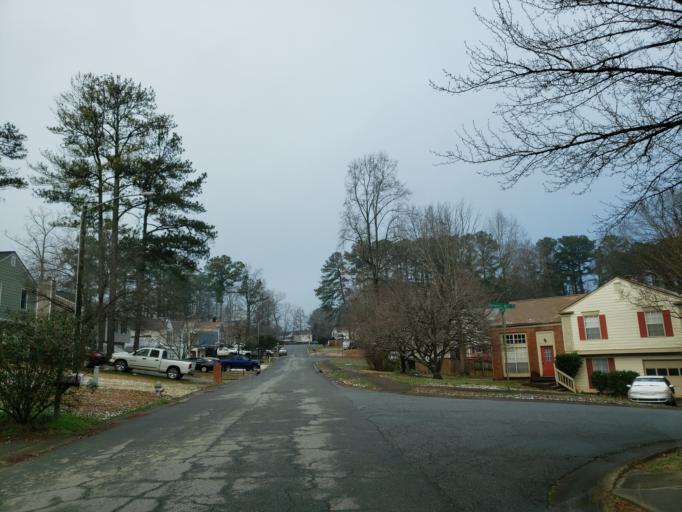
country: US
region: Georgia
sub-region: Cobb County
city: Kennesaw
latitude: 34.0237
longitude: -84.5985
